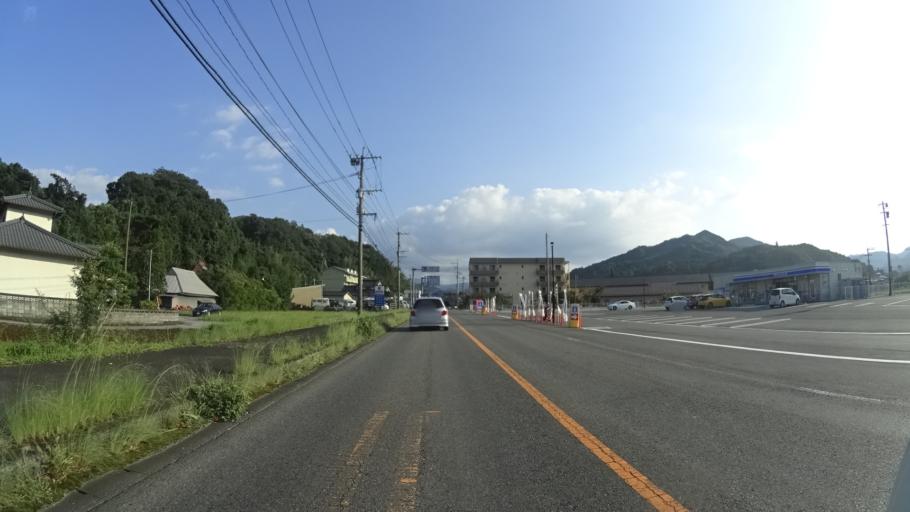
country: JP
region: Oita
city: Bungo-Takada-shi
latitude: 33.4554
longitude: 131.3288
